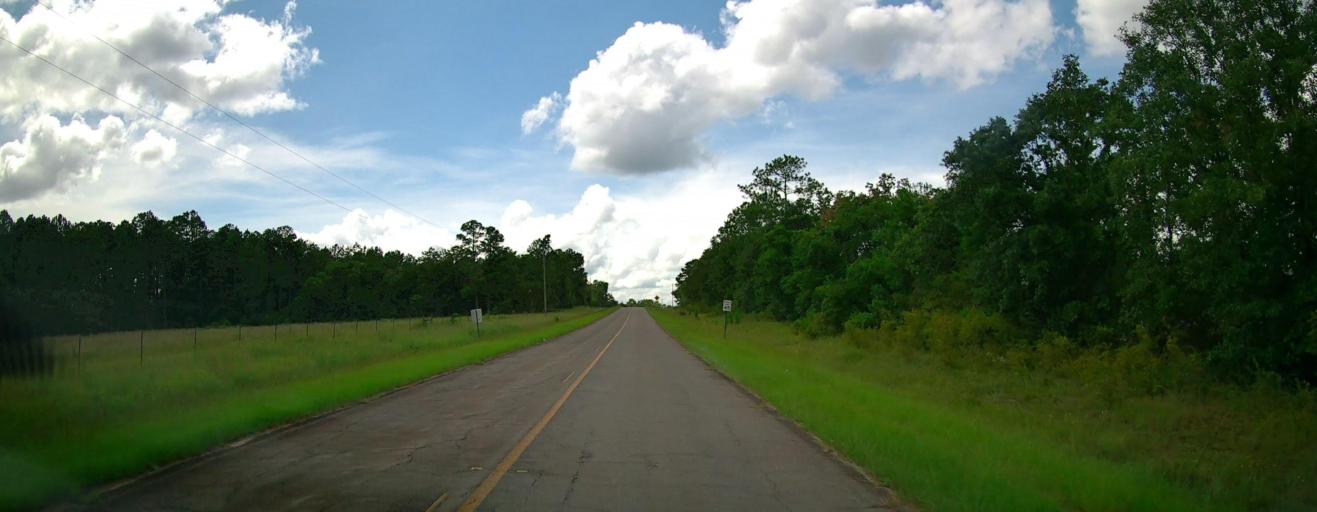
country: US
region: Georgia
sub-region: Taylor County
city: Butler
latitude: 32.5944
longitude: -84.3755
